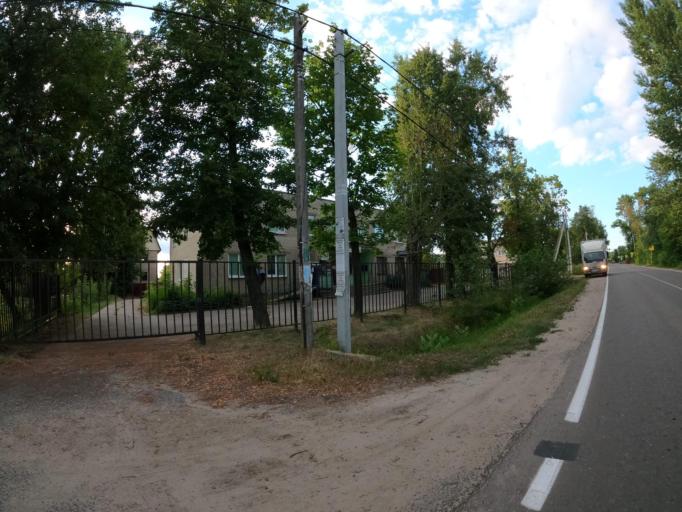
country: RU
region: Moskovskaya
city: Ashitkovo
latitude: 55.4223
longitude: 38.5513
